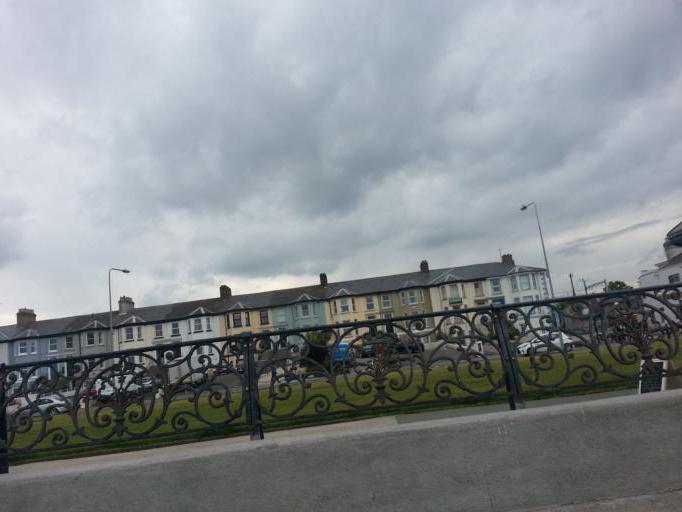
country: IE
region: Leinster
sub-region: Wicklow
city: Bray
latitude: 53.2029
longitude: -6.0976
